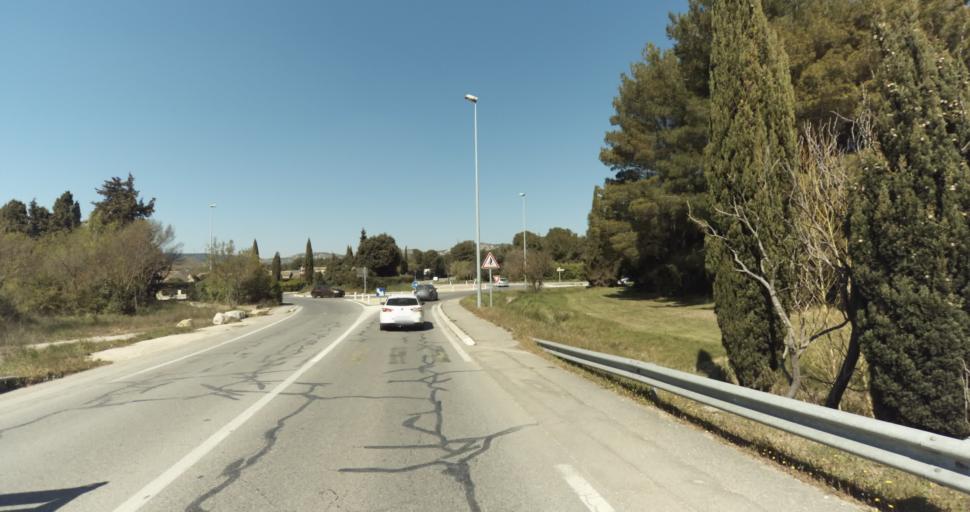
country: FR
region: Provence-Alpes-Cote d'Azur
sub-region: Departement des Bouches-du-Rhone
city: Pelissanne
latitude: 43.6292
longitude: 5.1660
